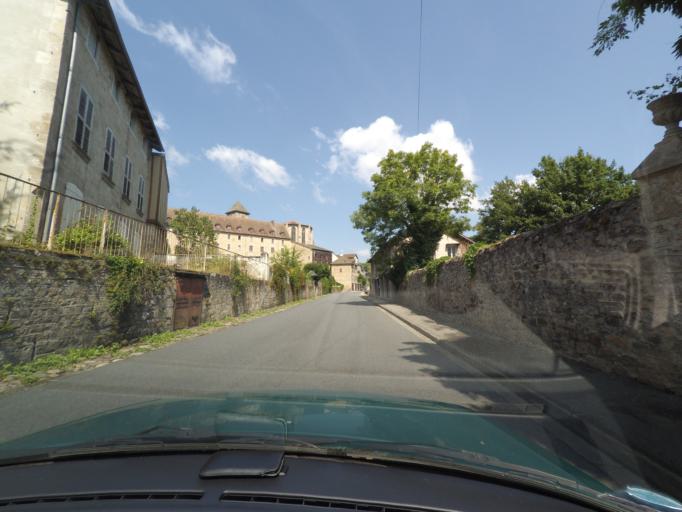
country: FR
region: Limousin
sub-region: Departement de la Haute-Vienne
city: Eymoutiers
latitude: 45.7381
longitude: 1.7458
